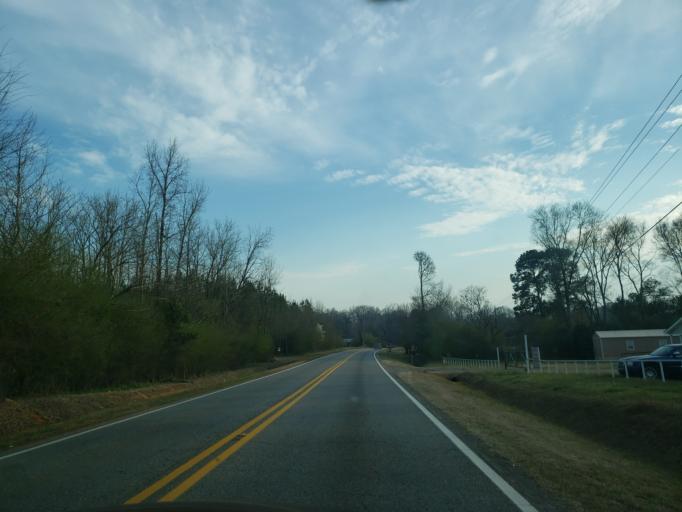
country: US
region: Alabama
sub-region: Hale County
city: Moundville
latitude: 32.9717
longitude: -87.6246
